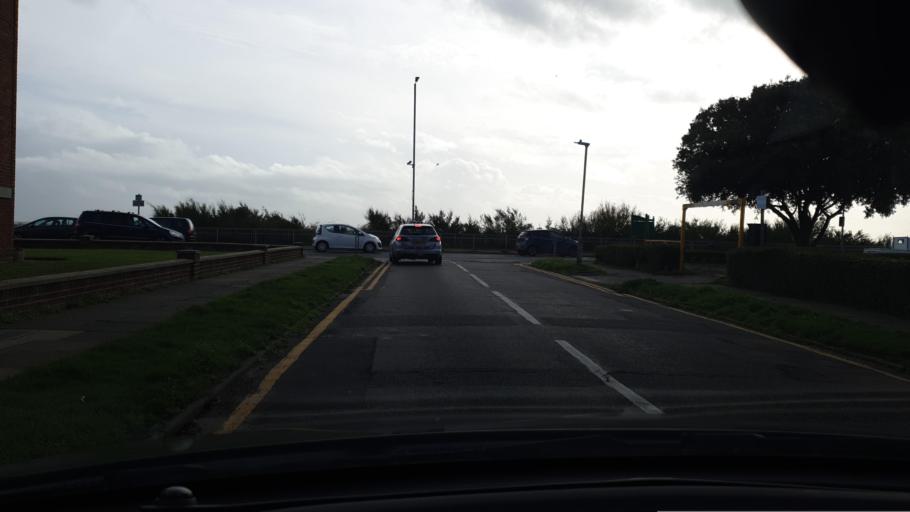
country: GB
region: England
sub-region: Essex
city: Clacton-on-Sea
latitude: 51.8006
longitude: 1.1913
